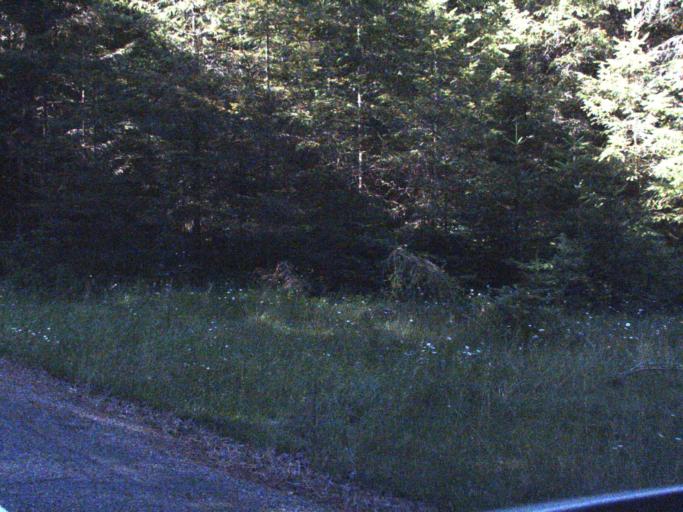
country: US
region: Washington
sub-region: King County
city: Riverbend
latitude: 47.1230
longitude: -121.6136
